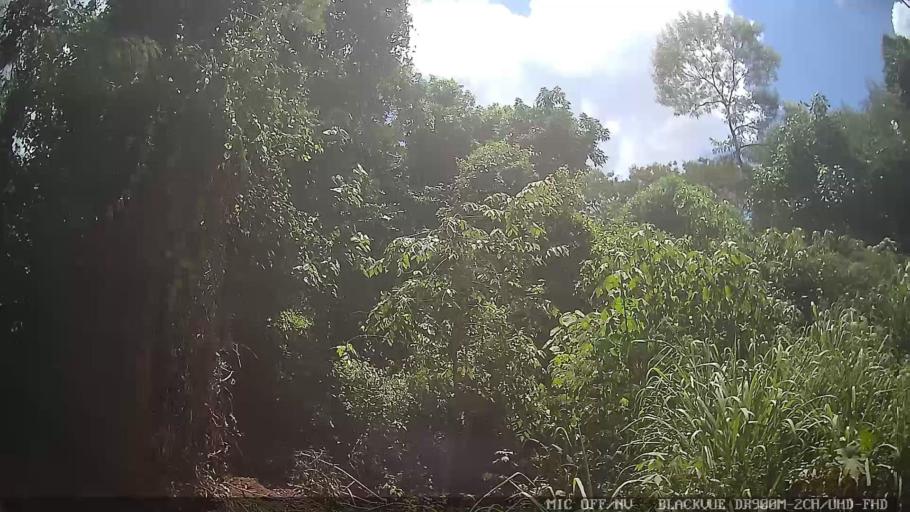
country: BR
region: Sao Paulo
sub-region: Jarinu
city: Jarinu
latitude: -23.1322
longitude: -46.6571
